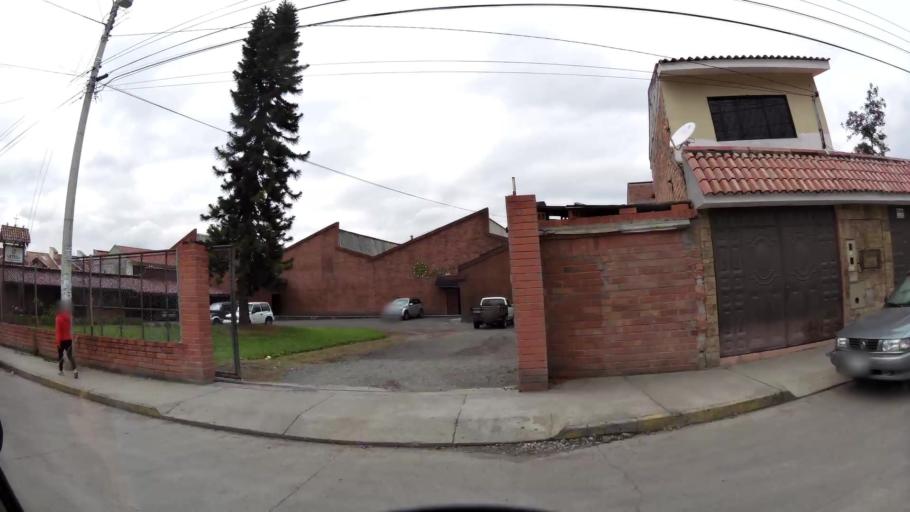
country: EC
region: Azuay
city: Cuenca
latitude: -2.9090
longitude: -79.0337
